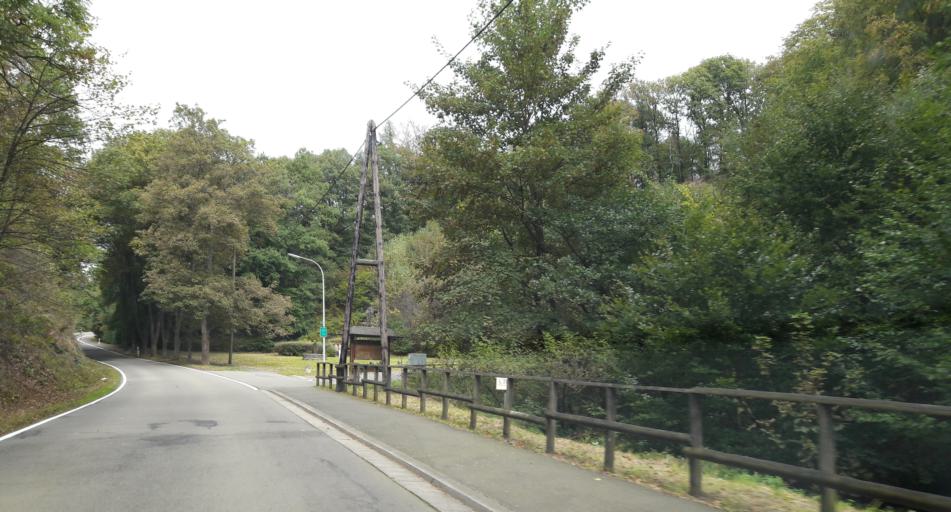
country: DE
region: Rheinland-Pfalz
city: Hahnweiler
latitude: 49.5189
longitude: 7.2112
